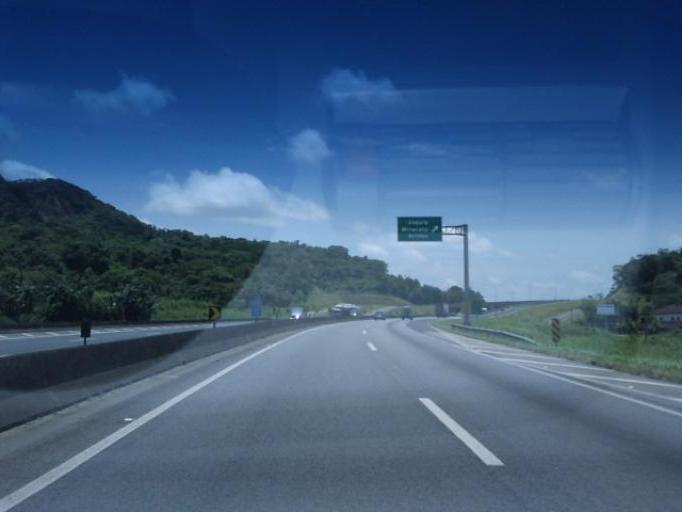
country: BR
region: Sao Paulo
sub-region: Juquia
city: Juquia
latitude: -24.3560
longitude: -47.6649
